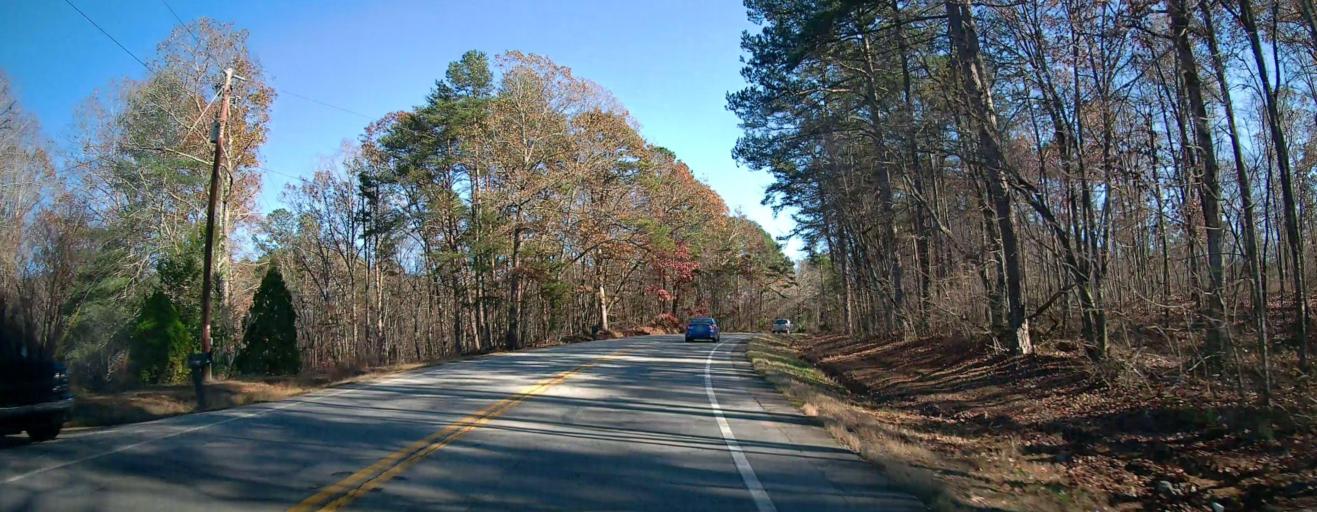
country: US
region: Georgia
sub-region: Hall County
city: Lula
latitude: 34.4062
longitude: -83.7010
